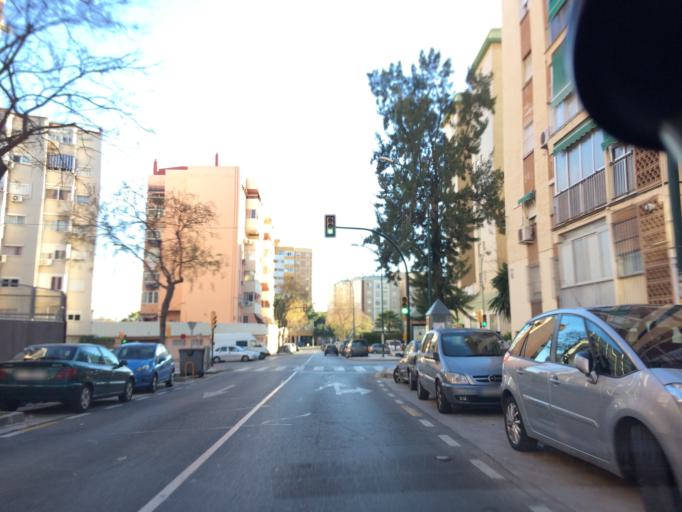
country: ES
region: Andalusia
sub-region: Provincia de Malaga
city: Malaga
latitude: 36.7231
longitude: -4.4419
